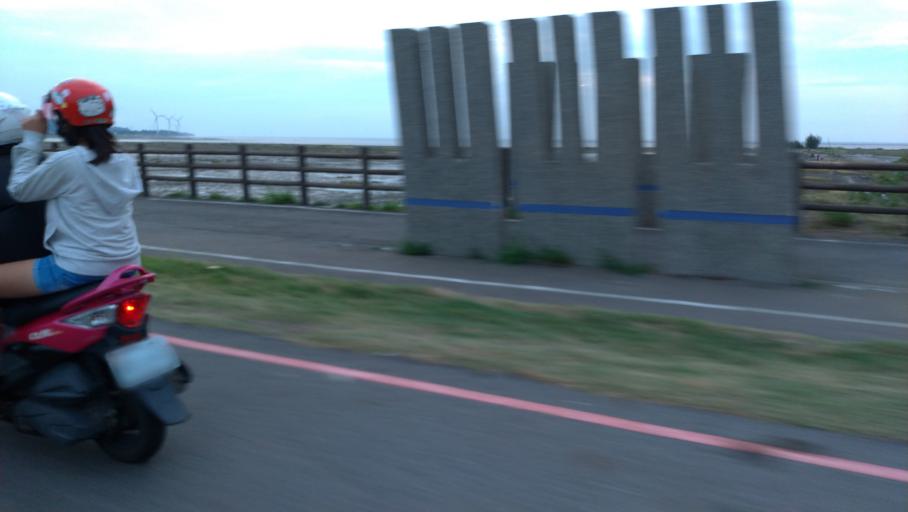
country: TW
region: Taiwan
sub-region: Hsinchu
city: Hsinchu
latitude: 24.7569
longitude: 120.9059
